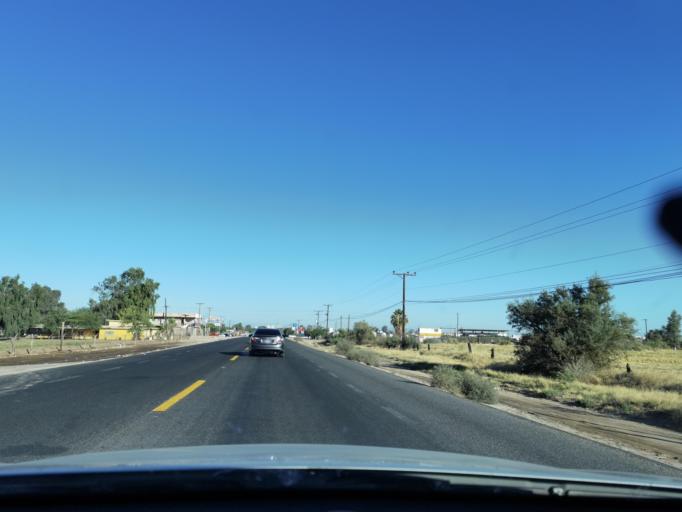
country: MX
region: Baja California
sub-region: Mexicali
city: Islas Agrarias Grupo A
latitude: 32.6466
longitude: -115.3247
